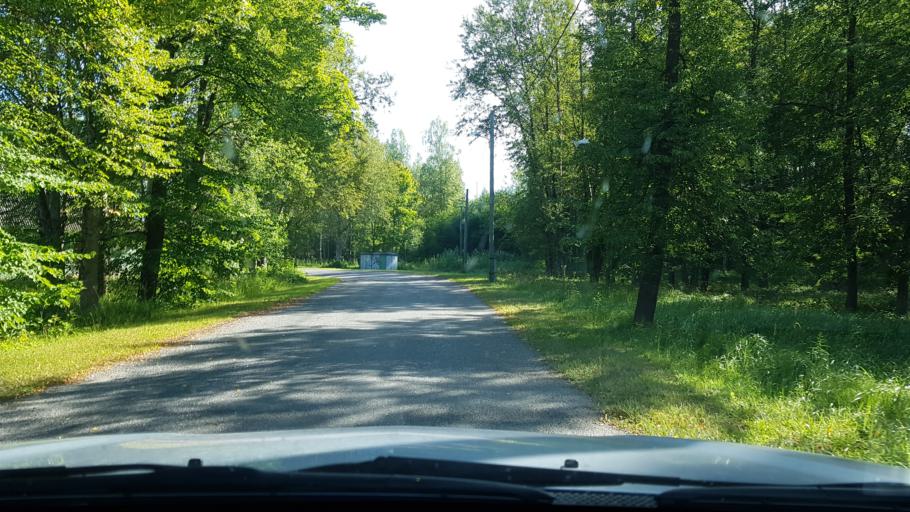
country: EE
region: Ida-Virumaa
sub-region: Sillamaee linn
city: Sillamae
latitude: 59.3376
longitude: 27.6918
